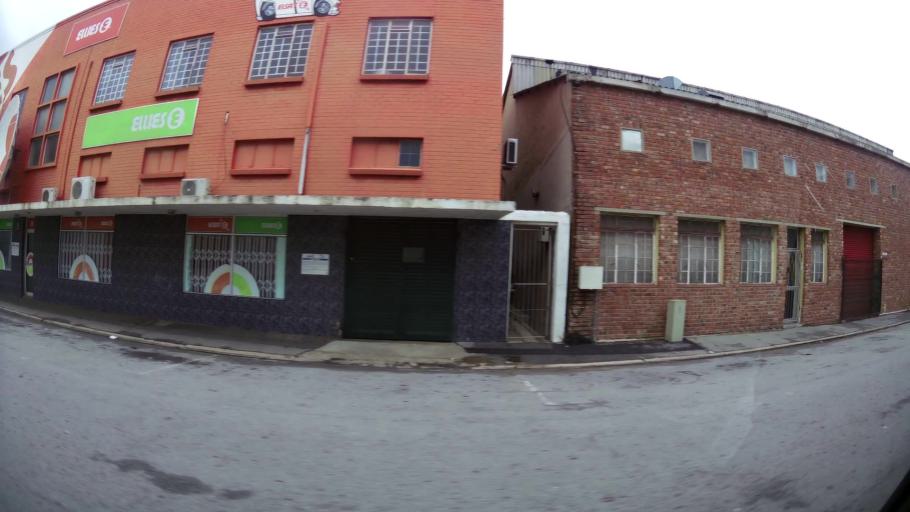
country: ZA
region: Eastern Cape
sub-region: Nelson Mandela Bay Metropolitan Municipality
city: Port Elizabeth
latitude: -33.9473
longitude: 25.6072
